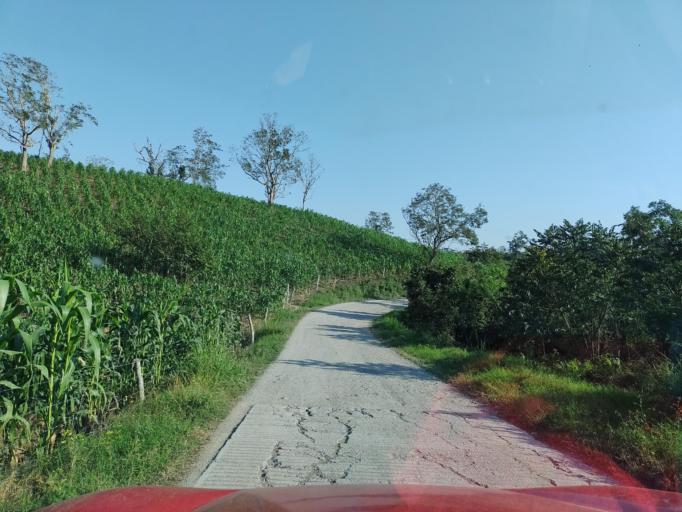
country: MX
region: Veracruz
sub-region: Papantla
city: Polutla
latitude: 20.4539
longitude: -97.2401
